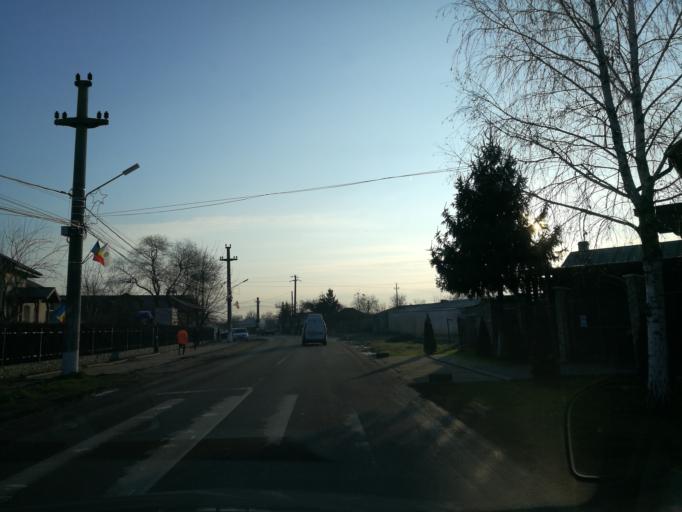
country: RO
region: Ilfov
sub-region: Comuna Moara Vlasiei
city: Moara Vlasiei
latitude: 44.6409
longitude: 26.2032
